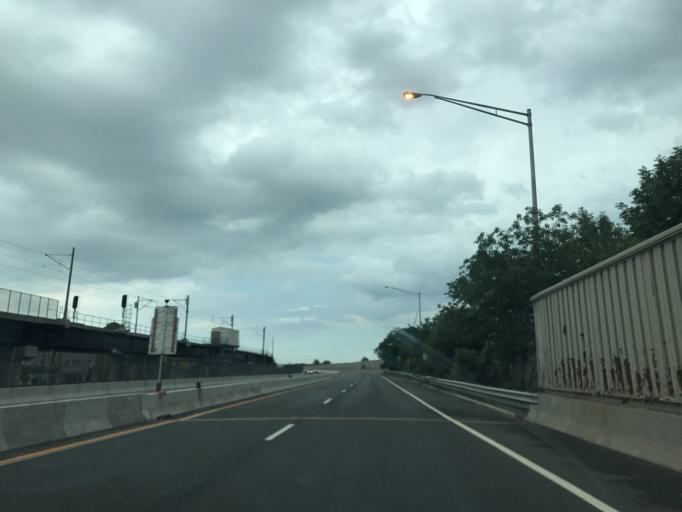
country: US
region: New Jersey
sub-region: Hudson County
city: Bayonne
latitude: 40.6541
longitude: -74.1296
